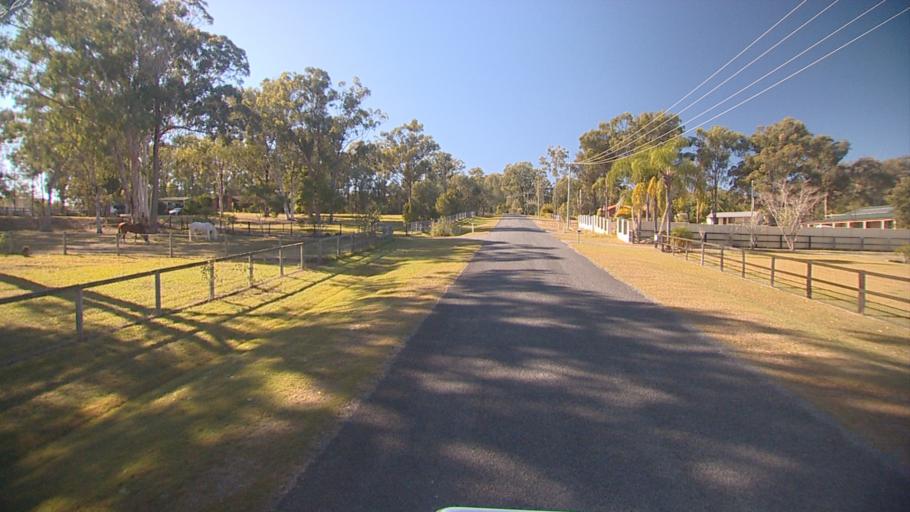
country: AU
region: Queensland
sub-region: Logan
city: Chambers Flat
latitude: -27.7920
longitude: 153.1297
